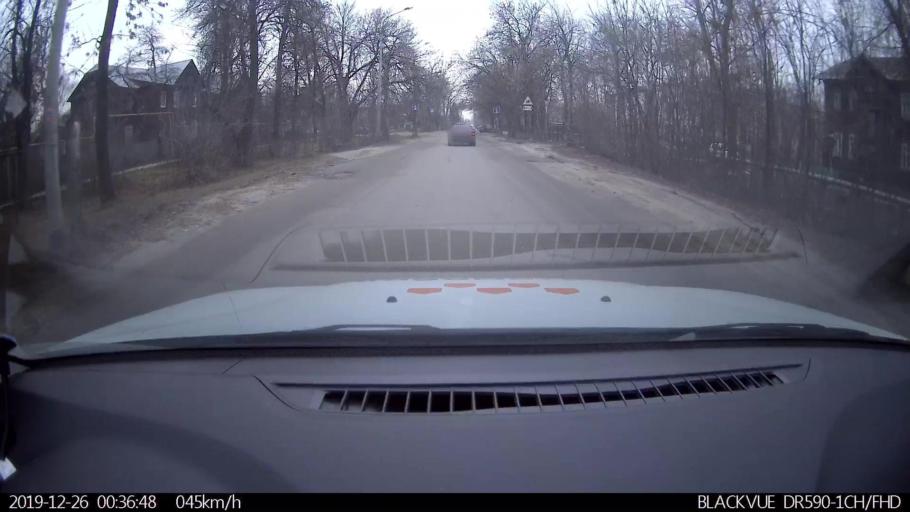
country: RU
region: Nizjnij Novgorod
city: Nizhniy Novgorod
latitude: 56.2914
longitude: 43.9060
